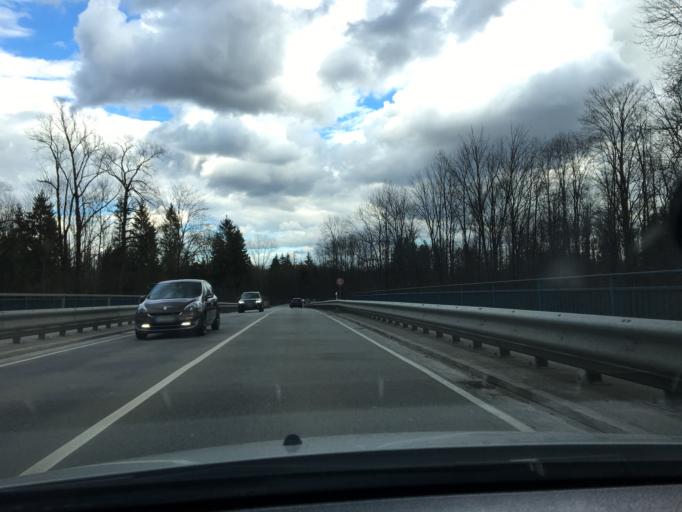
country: DE
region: Bavaria
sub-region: Upper Bavaria
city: Neufahrn bei Freising
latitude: 48.3131
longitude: 11.6997
